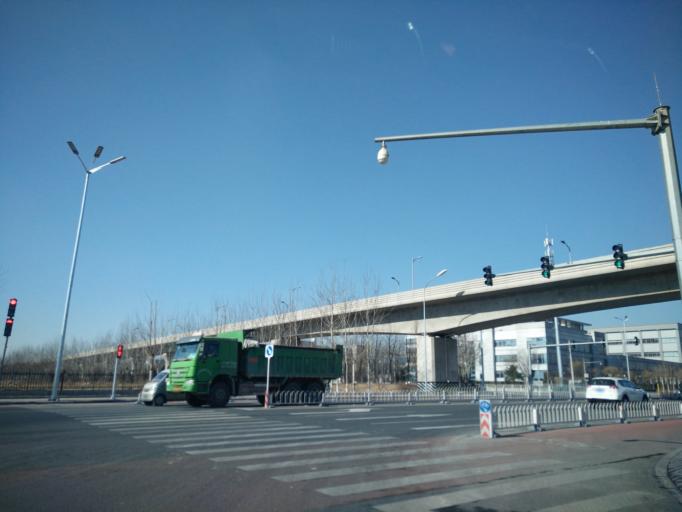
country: CN
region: Beijing
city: Jiugong
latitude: 39.7748
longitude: 116.5413
